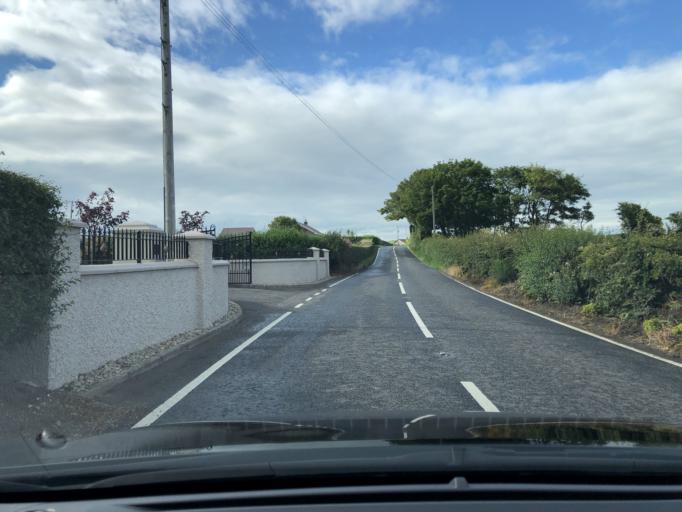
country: GB
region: Northern Ireland
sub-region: Down District
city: Dundrum
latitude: 54.2614
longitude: -5.7824
